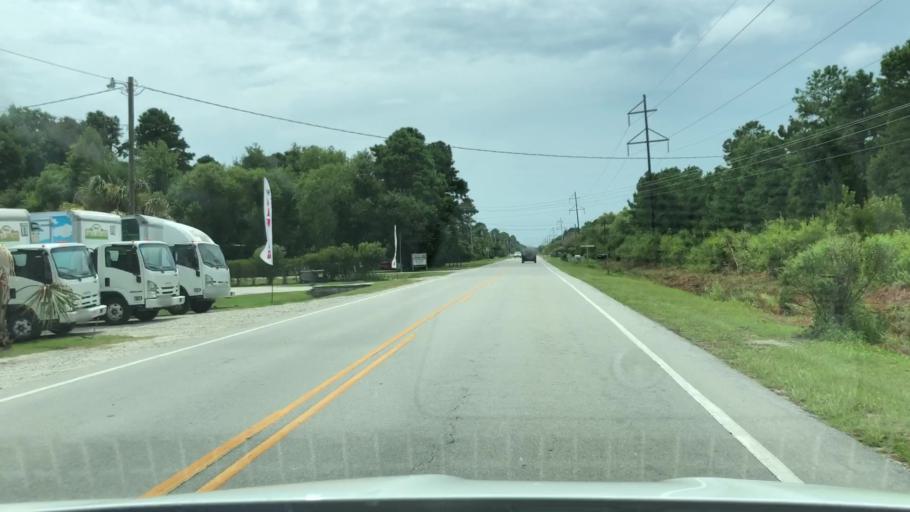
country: US
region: North Carolina
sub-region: Carteret County
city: Newport
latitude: 34.7533
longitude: -76.8760
